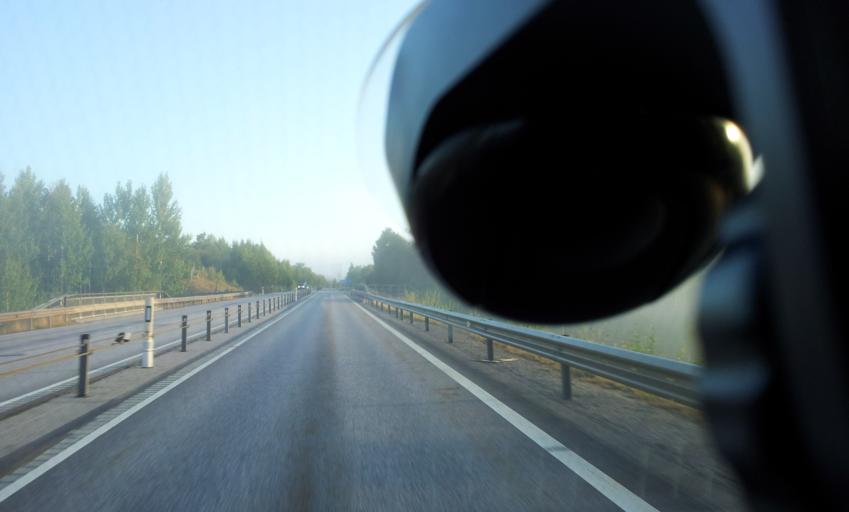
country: SE
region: Kalmar
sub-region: Vasterviks Kommun
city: Vaestervik
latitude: 57.7545
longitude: 16.5571
